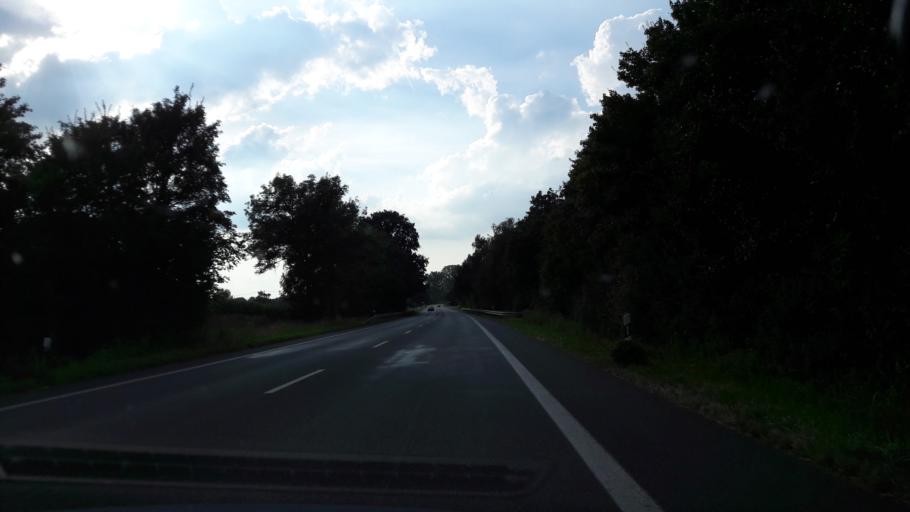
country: DE
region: North Rhine-Westphalia
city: Sendenhorst
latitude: 51.8309
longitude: 7.8748
